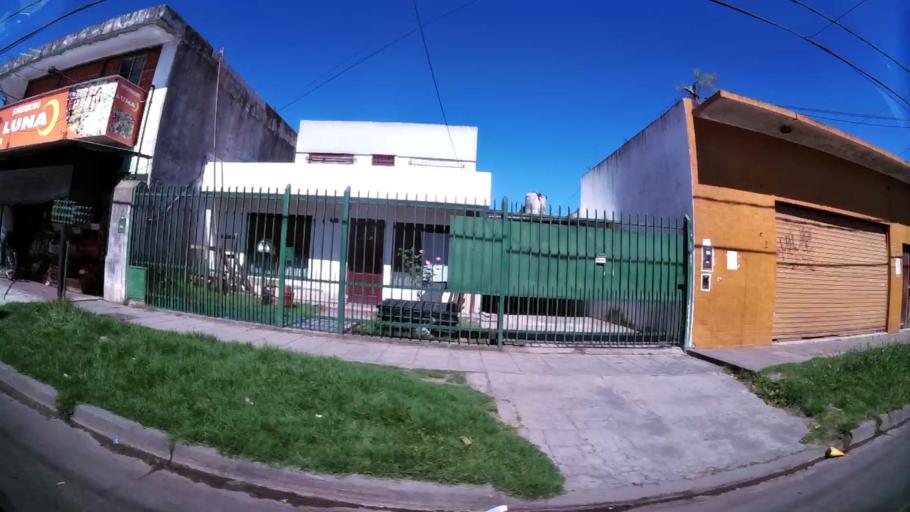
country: AR
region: Buenos Aires
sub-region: Partido de Tigre
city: Tigre
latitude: -34.4922
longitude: -58.6125
